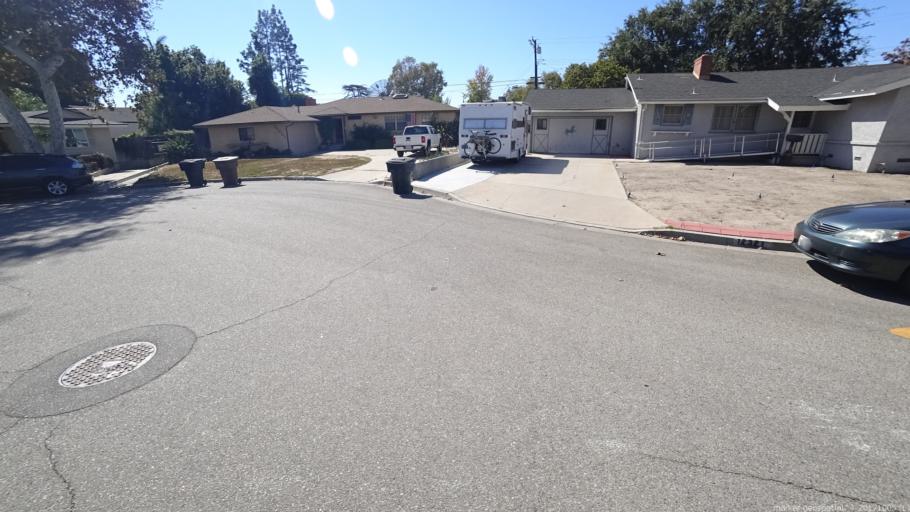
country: US
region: California
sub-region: Orange County
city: Garden Grove
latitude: 33.7837
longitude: -117.9625
